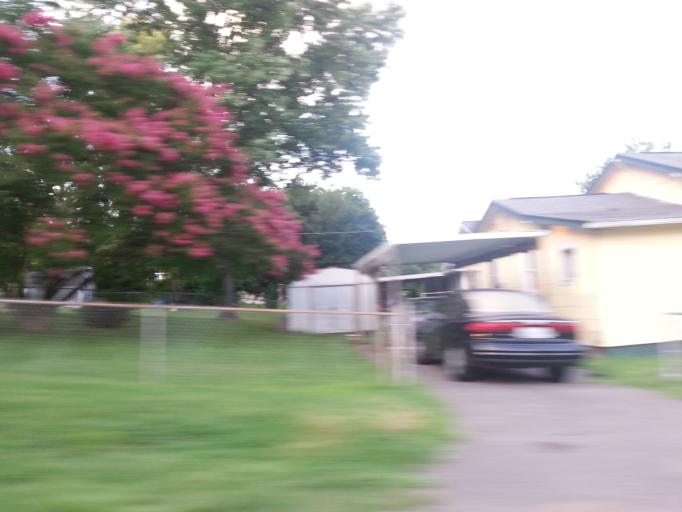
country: US
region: Tennessee
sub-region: Knox County
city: Knoxville
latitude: 35.9992
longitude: -83.9143
